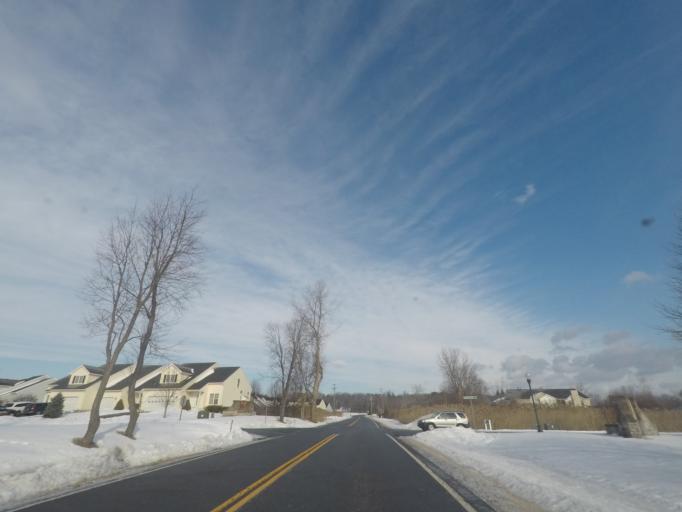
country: US
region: New York
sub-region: Saratoga County
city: Mechanicville
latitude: 42.8612
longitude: -73.7358
